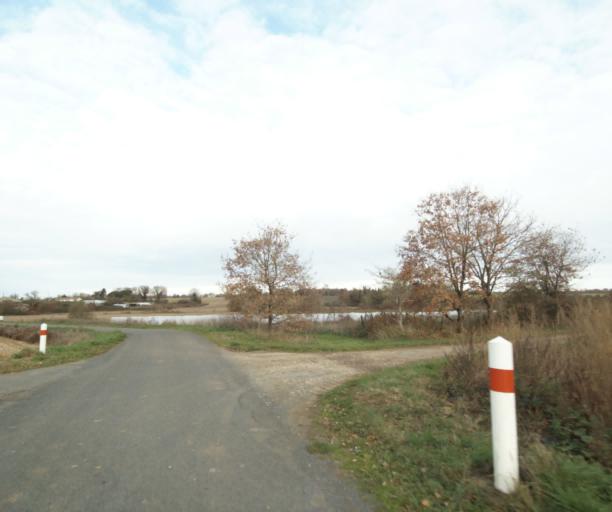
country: FR
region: Poitou-Charentes
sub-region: Departement de la Charente-Maritime
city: Saint-Porchaire
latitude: 45.7908
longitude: -0.8116
